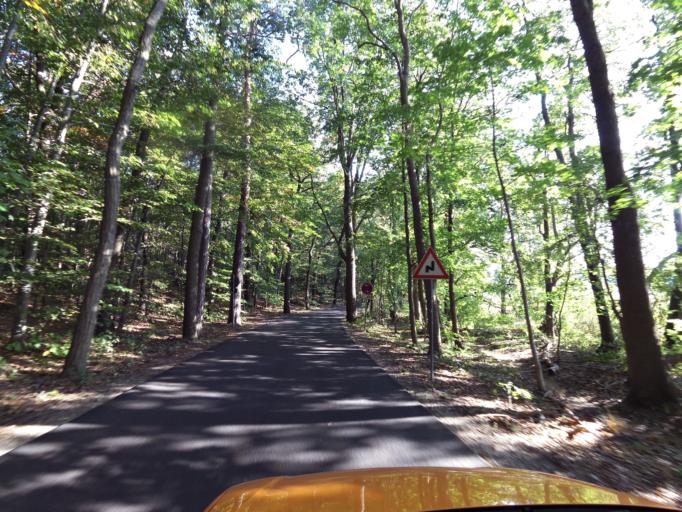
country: DE
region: Brandenburg
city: Potsdam
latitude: 52.4482
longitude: 13.0680
